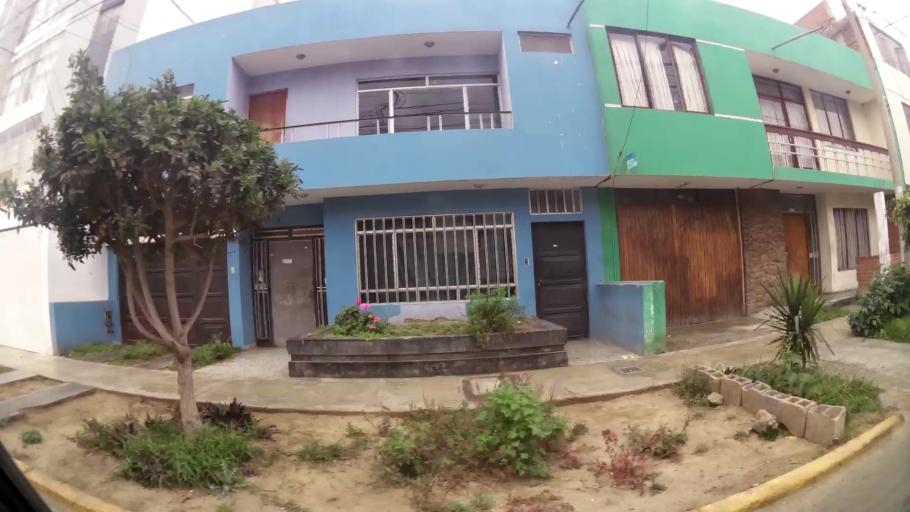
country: PE
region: La Libertad
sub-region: Provincia de Trujillo
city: Trujillo
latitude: -8.1158
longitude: -79.0364
